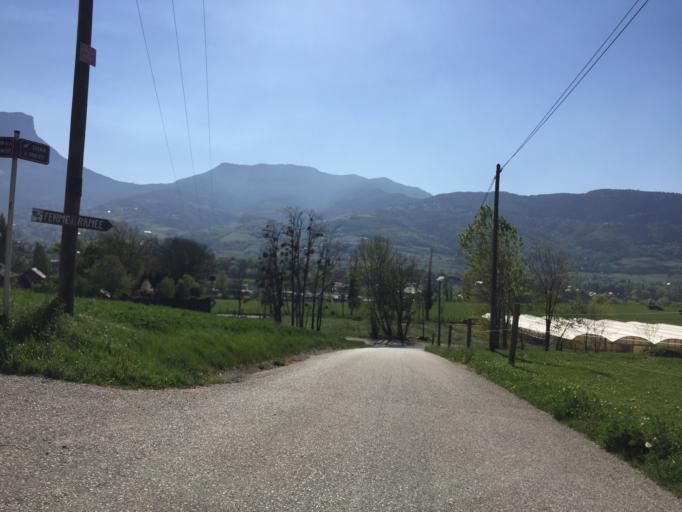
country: FR
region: Rhone-Alpes
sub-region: Departement de la Savoie
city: Challes-les-Eaux
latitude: 45.5282
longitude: 5.9821
